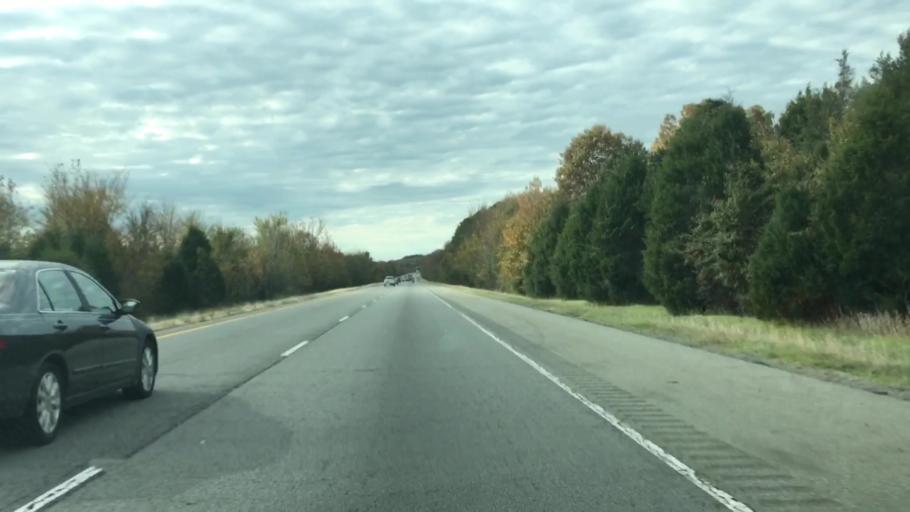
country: US
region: Arkansas
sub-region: Faulkner County
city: Conway
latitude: 35.1202
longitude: -92.4755
